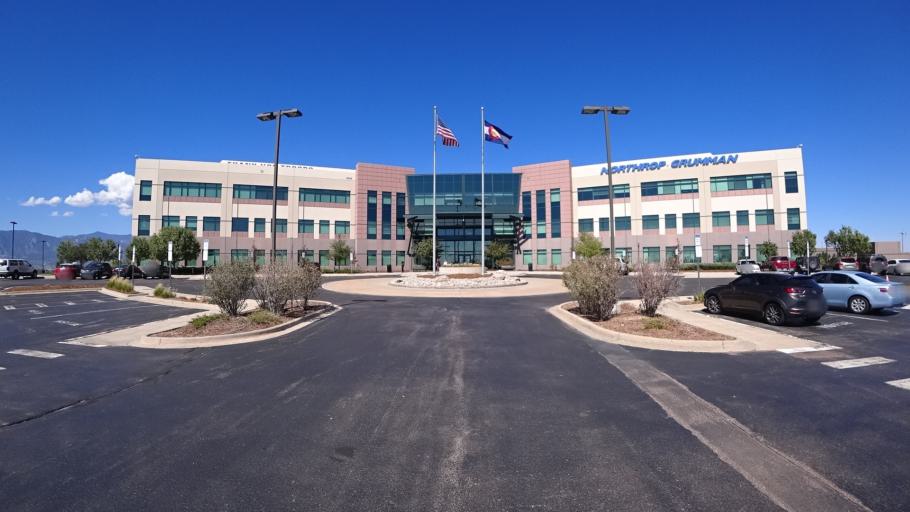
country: US
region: Colorado
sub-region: El Paso County
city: Security-Widefield
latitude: 38.7791
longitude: -104.7014
